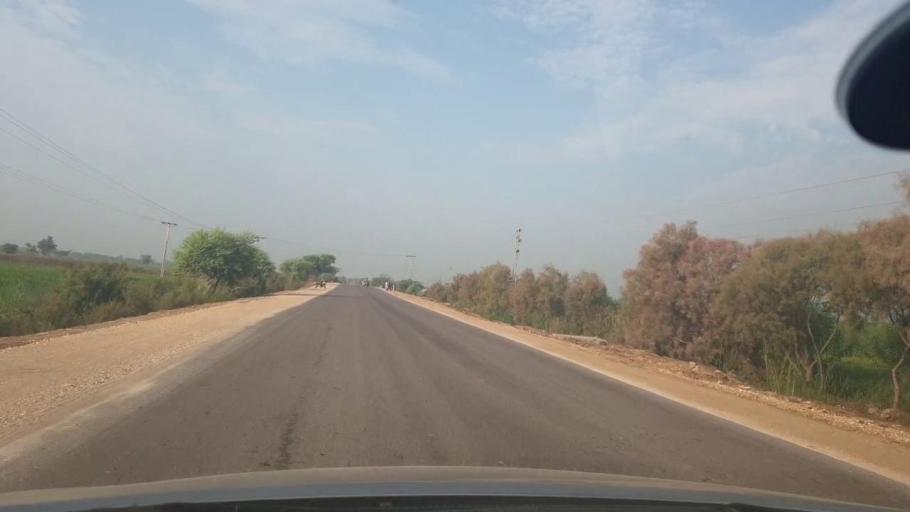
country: PK
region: Sindh
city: Jacobabad
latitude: 28.2519
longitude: 68.4057
